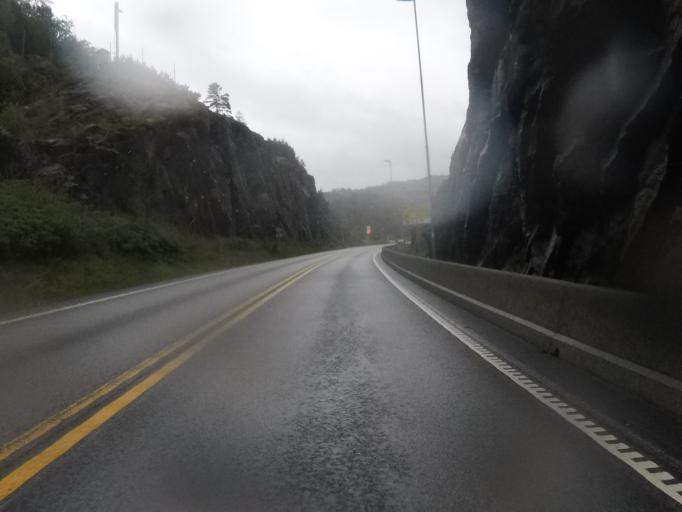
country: NO
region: Vest-Agder
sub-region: Kvinesdal
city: Liknes
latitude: 58.2210
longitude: 7.0079
